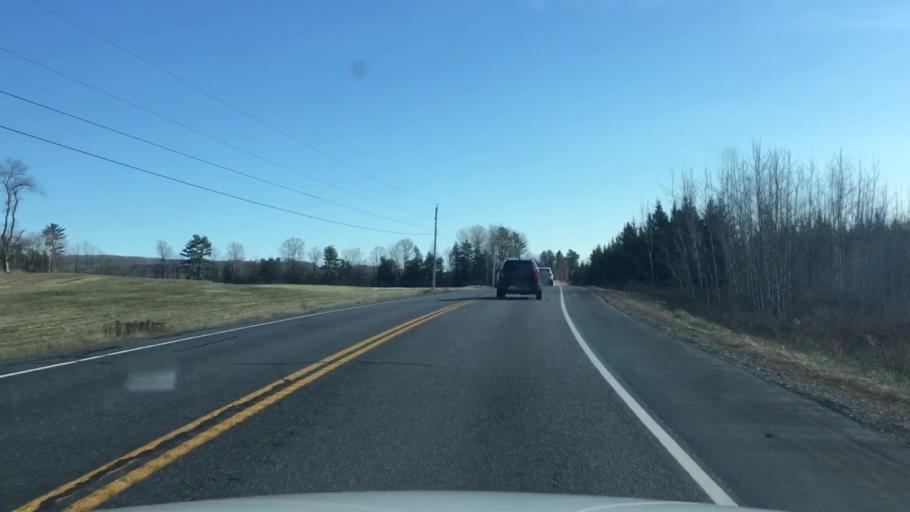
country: US
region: Maine
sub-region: Knox County
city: Washington
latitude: 44.2387
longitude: -69.3598
